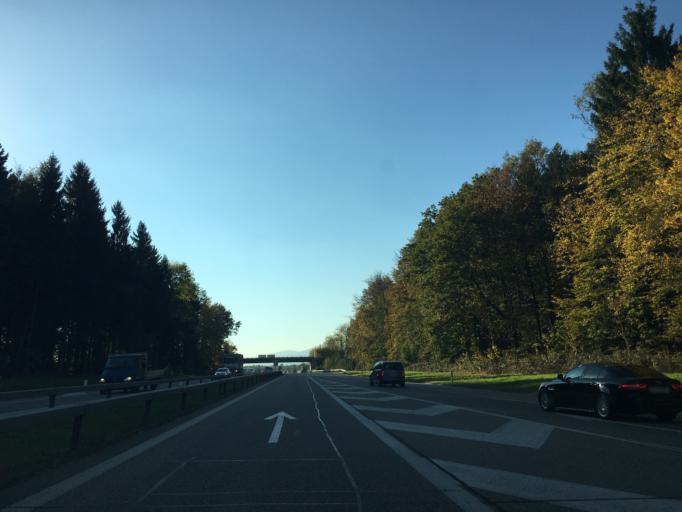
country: CH
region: Solothurn
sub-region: Bezirk Wasseramt
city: Luterbach
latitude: 47.2102
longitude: 7.5970
